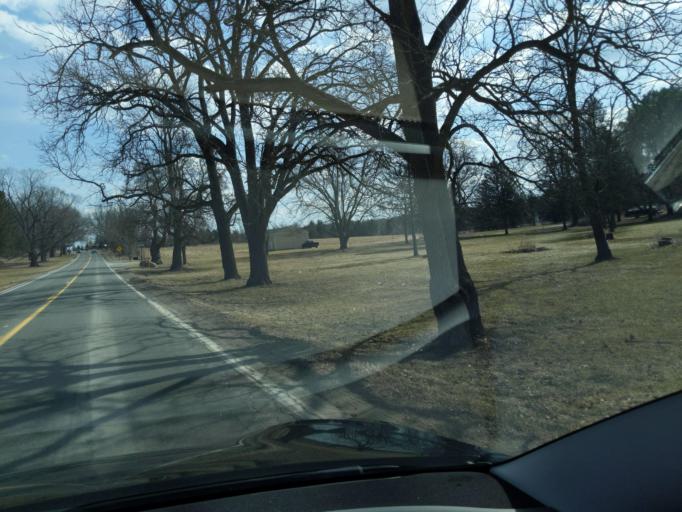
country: US
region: Michigan
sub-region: Washtenaw County
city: Dexter
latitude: 42.3846
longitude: -83.8967
